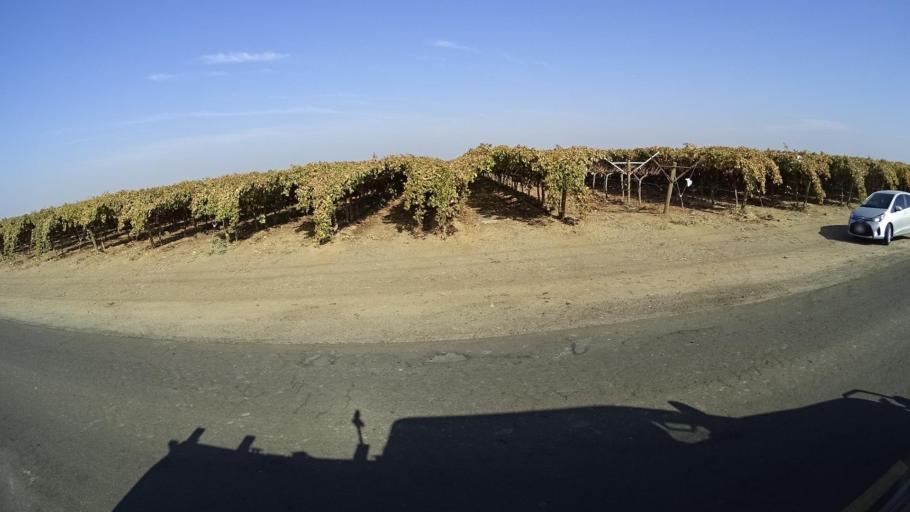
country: US
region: California
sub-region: Kern County
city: McFarland
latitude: 35.6892
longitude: -119.1833
